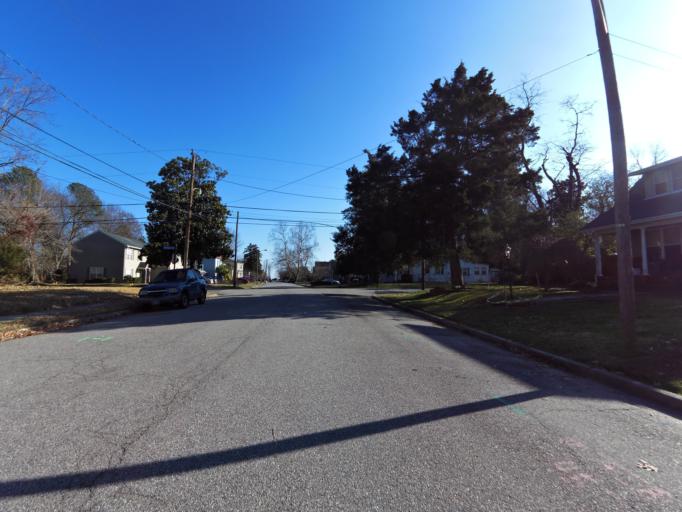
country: US
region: Virginia
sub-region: City of Newport News
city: Newport News
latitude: 36.9963
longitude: -76.3854
